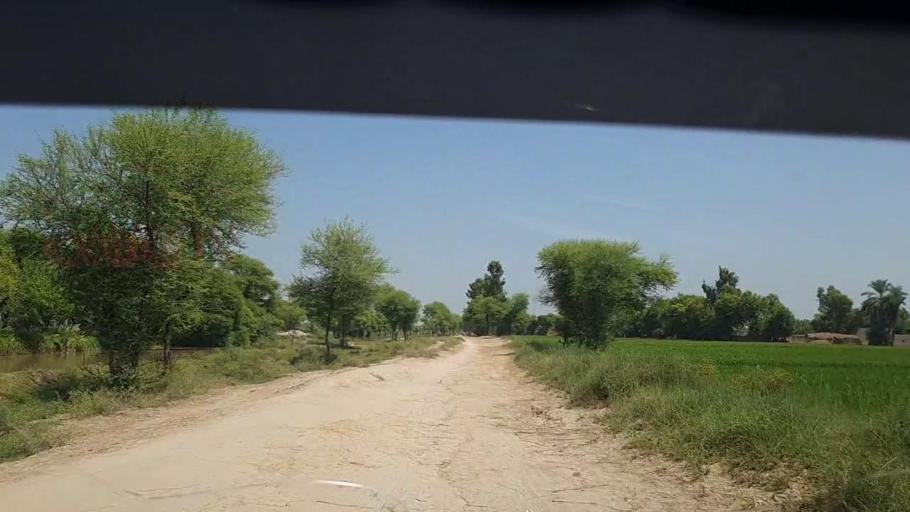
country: PK
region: Sindh
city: Tangwani
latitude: 28.2329
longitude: 68.9576
